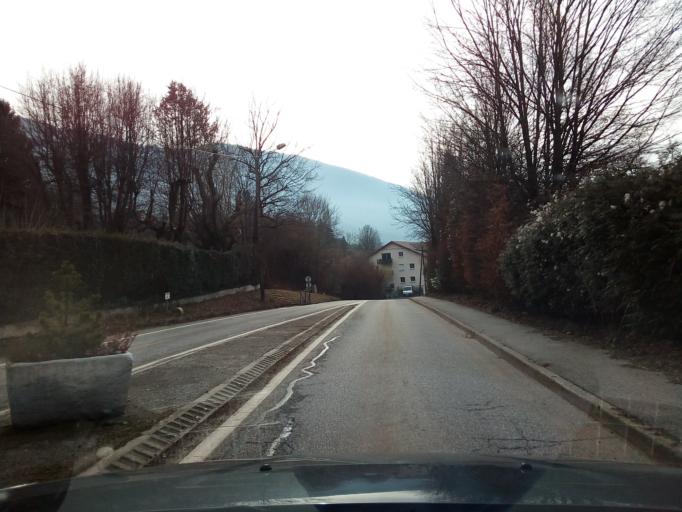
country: FR
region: Rhone-Alpes
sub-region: Departement de l'Isere
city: Vaulnaveys-le-Haut
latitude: 45.1483
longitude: 5.8375
